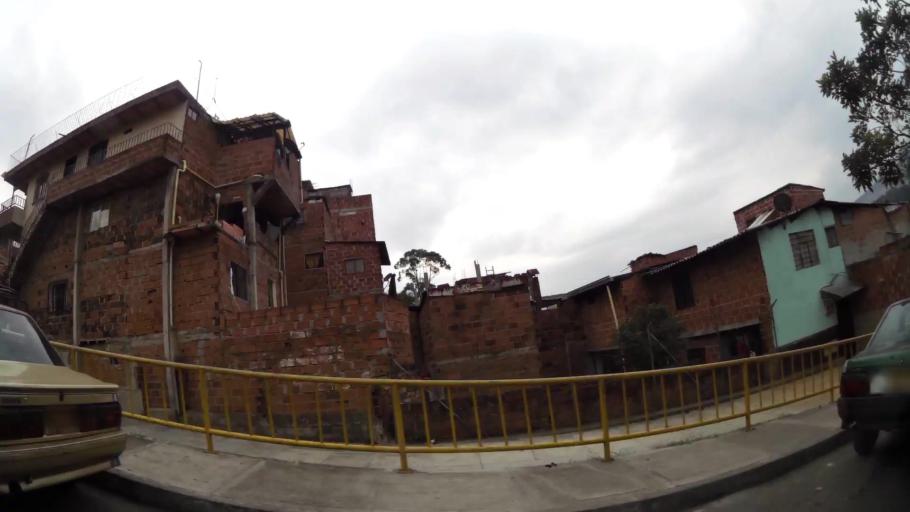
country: CO
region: Antioquia
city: Bello
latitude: 6.3051
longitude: -75.5555
